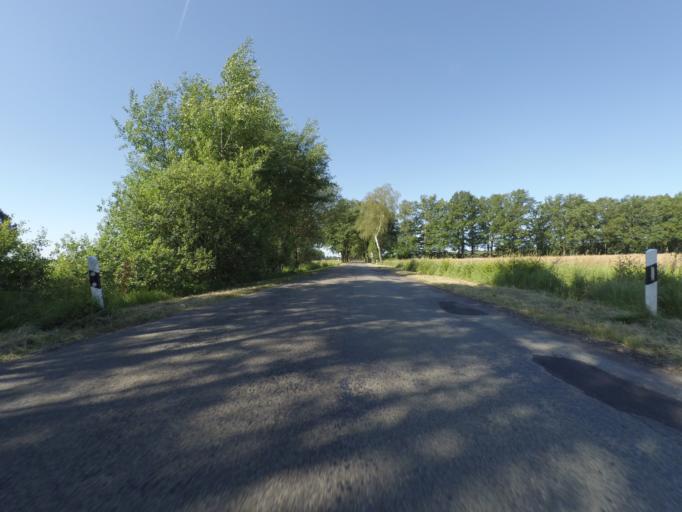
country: DE
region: Brandenburg
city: Triglitz
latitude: 53.2116
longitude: 12.0796
